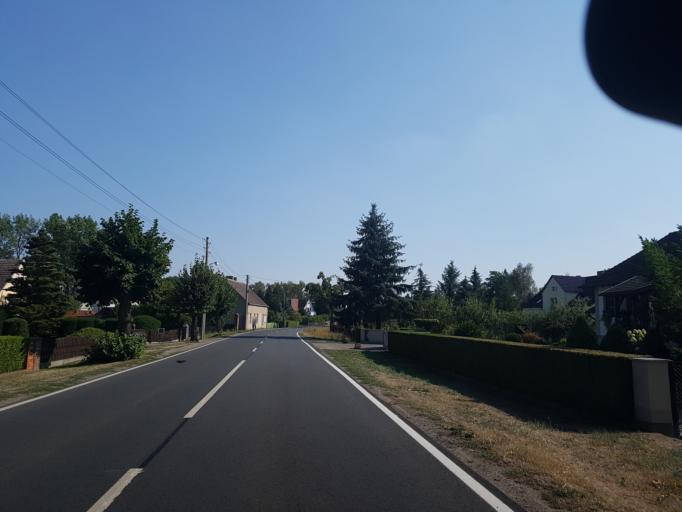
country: DE
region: Saxony-Anhalt
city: Annaburg
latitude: 51.7388
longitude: 13.0416
